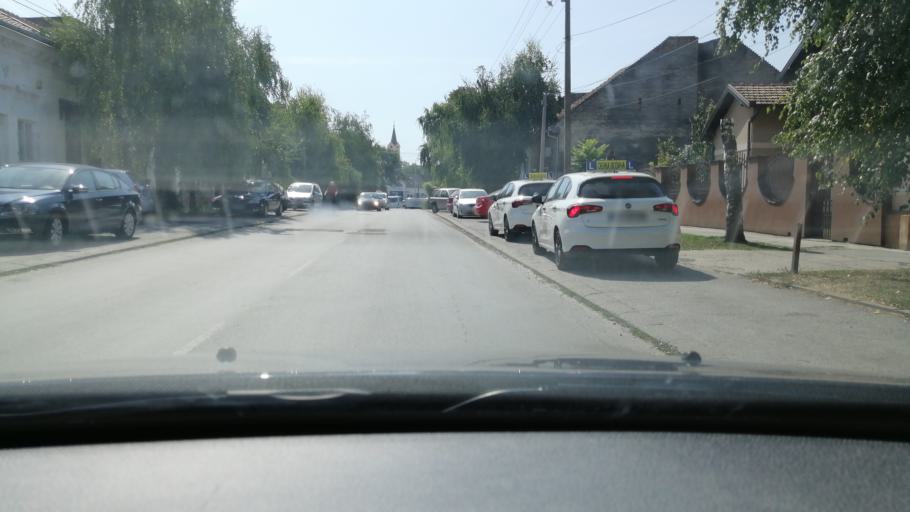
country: RS
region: Autonomna Pokrajina Vojvodina
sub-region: Srednjebanatski Okrug
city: Zrenjanin
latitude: 45.3845
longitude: 20.3878
